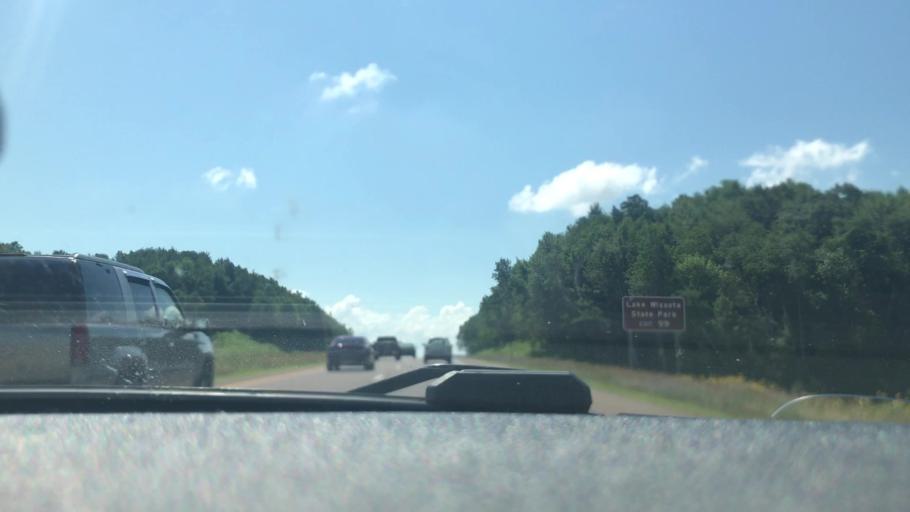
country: US
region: Wisconsin
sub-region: Chippewa County
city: Chippewa Falls
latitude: 44.9780
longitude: -91.4369
